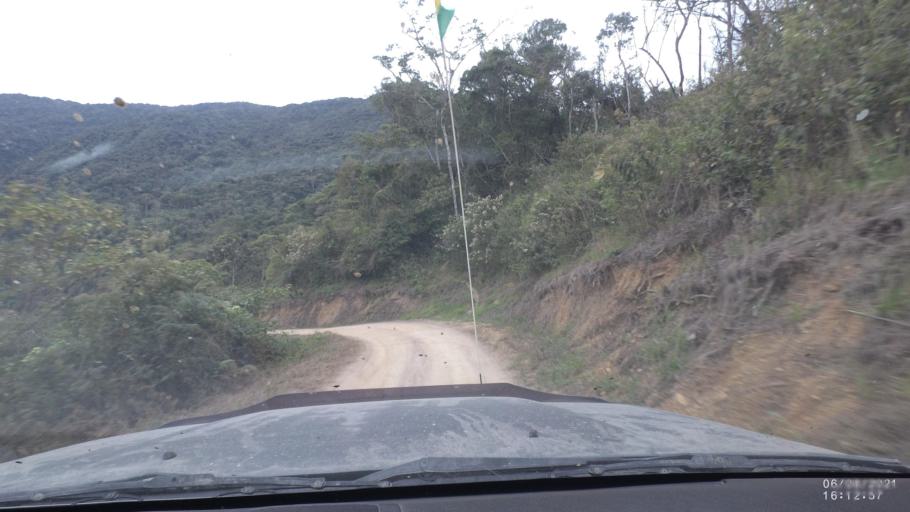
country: BO
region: La Paz
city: Quime
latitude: -16.5559
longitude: -66.7378
